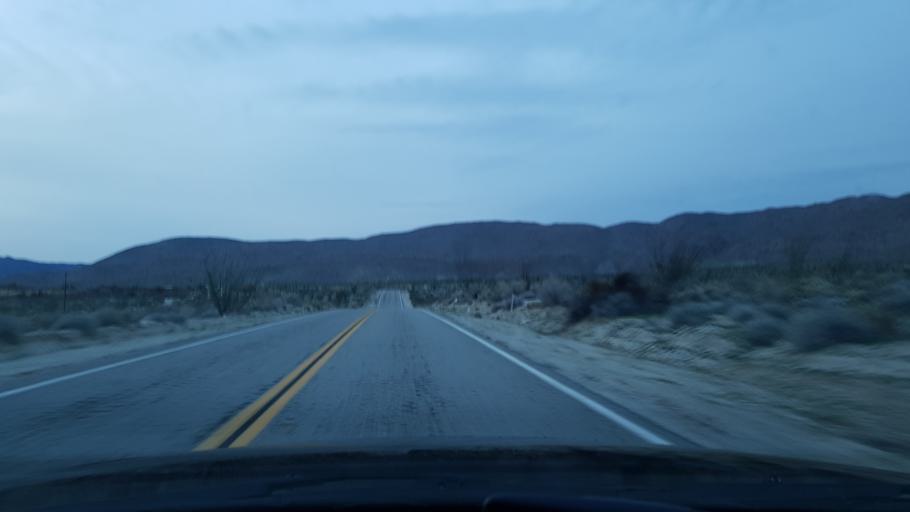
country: US
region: California
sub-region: San Diego County
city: Pine Valley
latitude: 32.9728
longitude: -116.3423
